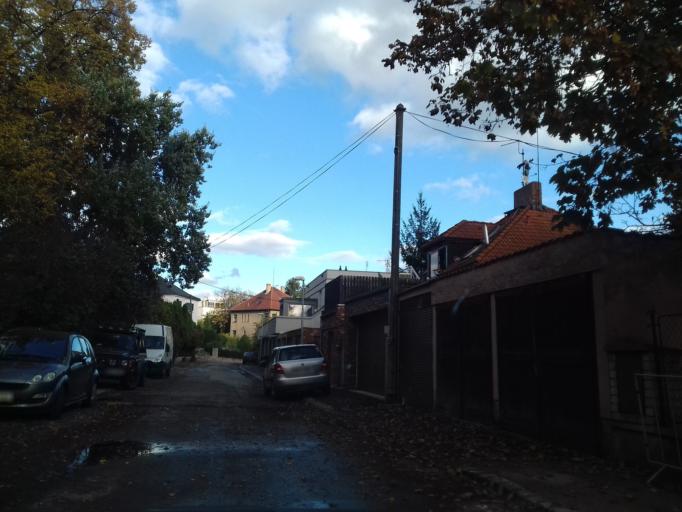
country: CZ
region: Praha
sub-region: Praha 4
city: Hodkovicky
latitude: 50.0248
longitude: 14.4084
